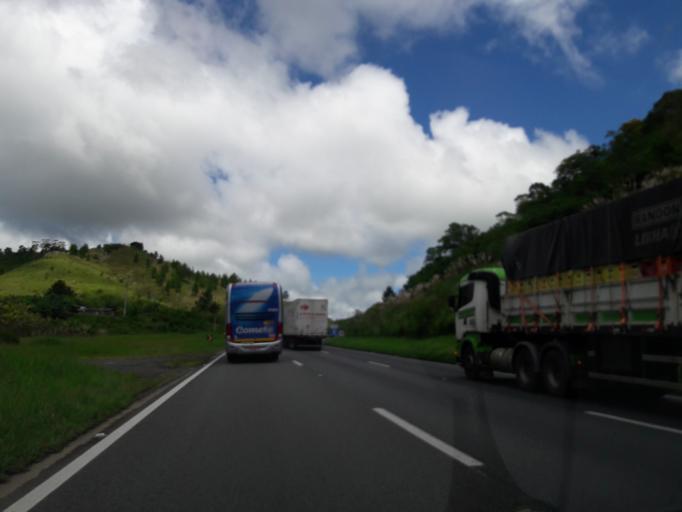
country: BR
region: Sao Paulo
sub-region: Cajati
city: Cajati
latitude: -24.9669
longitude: -48.4884
